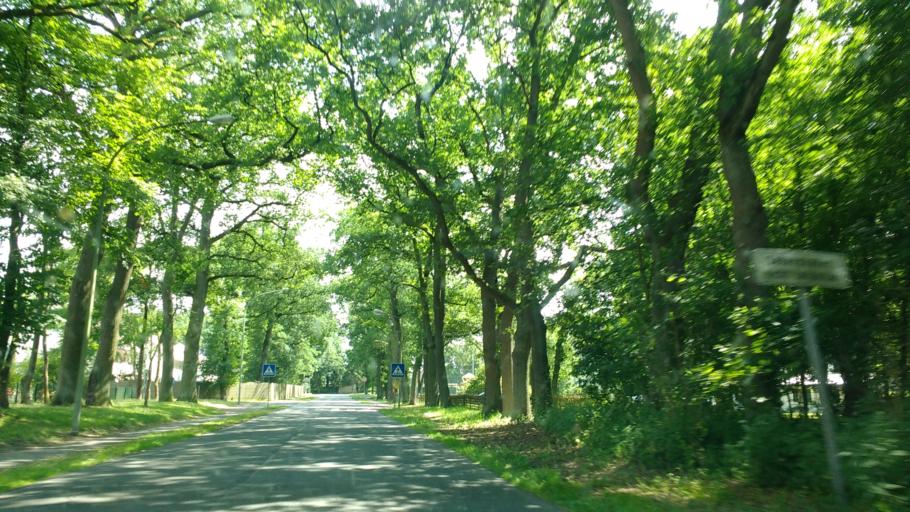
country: DE
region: North Rhine-Westphalia
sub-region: Regierungsbezirk Detmold
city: Paderborn
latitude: 51.7694
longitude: 8.7271
